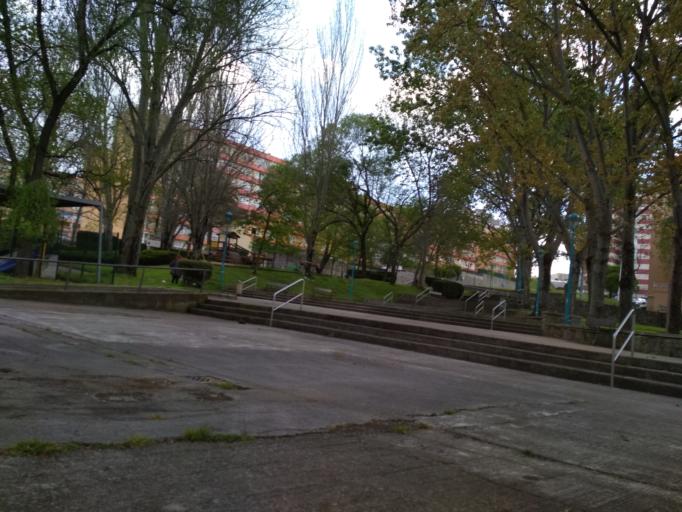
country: ES
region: Galicia
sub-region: Provincia da Coruna
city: A Coruna
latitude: 43.3447
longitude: -8.4025
